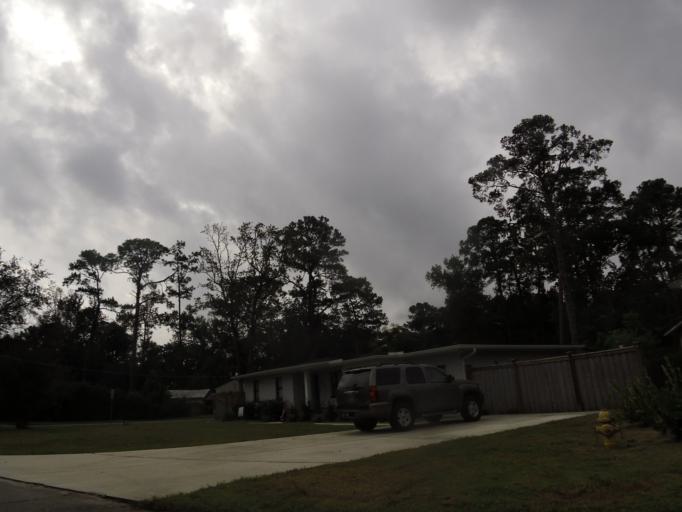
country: US
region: Florida
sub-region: Clay County
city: Bellair-Meadowbrook Terrace
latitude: 30.2501
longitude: -81.7008
